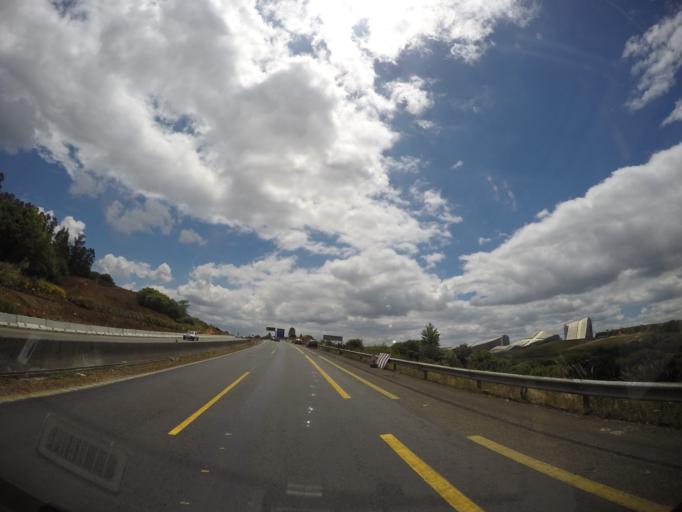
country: ES
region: Galicia
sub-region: Provincia da Coruna
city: Negreira
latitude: 42.8376
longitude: -8.7243
